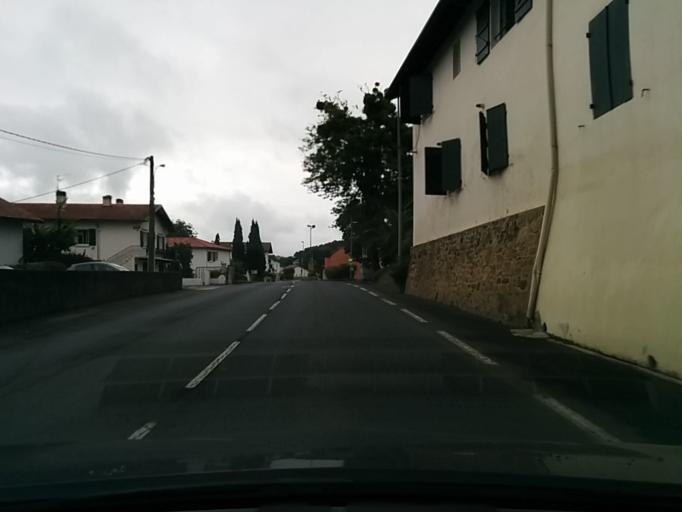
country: FR
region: Aquitaine
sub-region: Departement des Pyrenees-Atlantiques
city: Saint-Pee-sur-Nivelle
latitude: 43.3366
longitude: -1.5492
